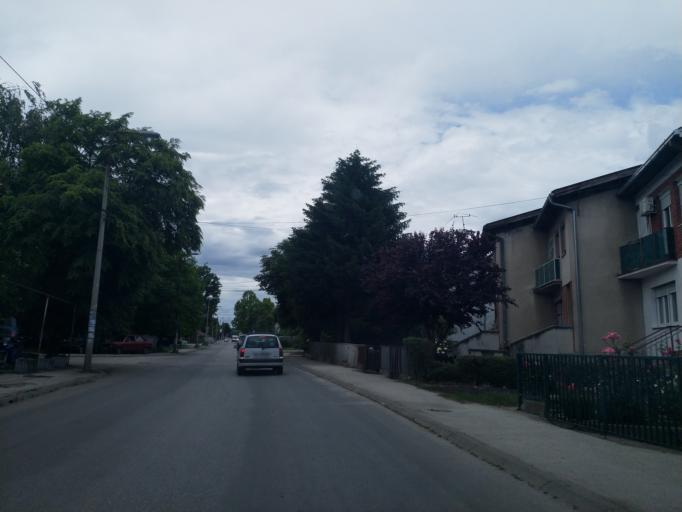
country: RS
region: Central Serbia
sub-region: Pomoravski Okrug
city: Jagodina
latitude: 43.9753
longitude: 21.2723
